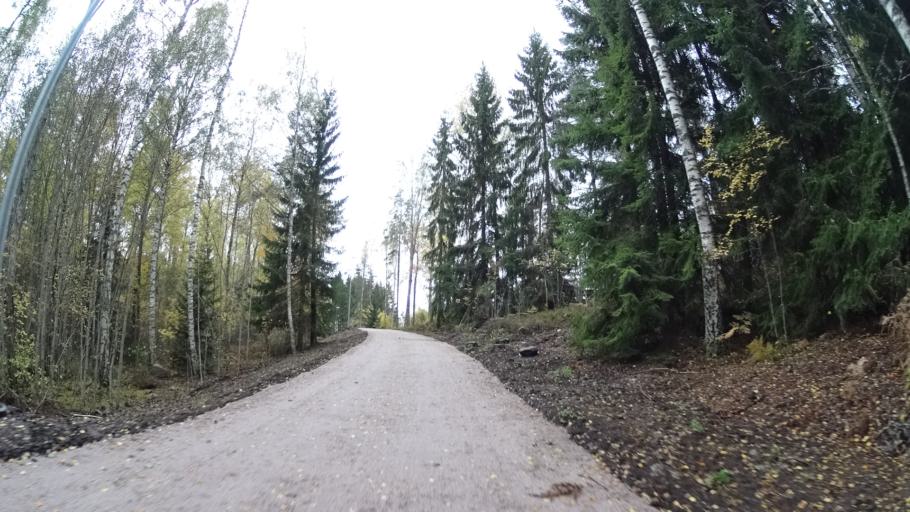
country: FI
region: Uusimaa
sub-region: Helsinki
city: Espoo
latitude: 60.2319
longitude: 24.6471
